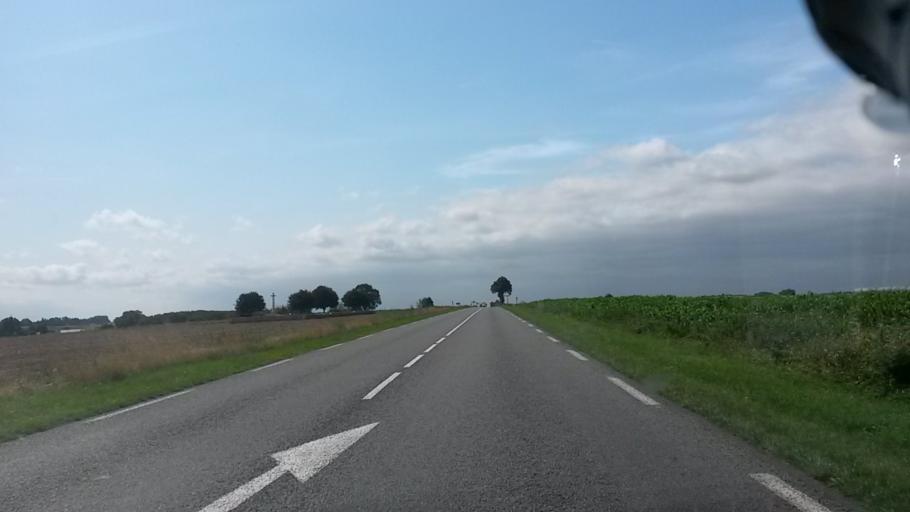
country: FR
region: Nord-Pas-de-Calais
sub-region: Departement du Pas-de-Calais
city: Hermies
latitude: 50.1314
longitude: 2.9901
